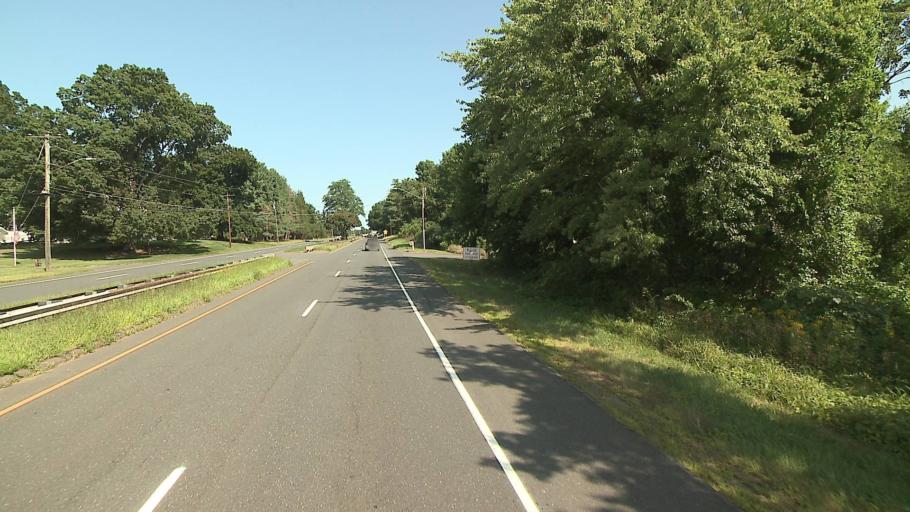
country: US
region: Connecticut
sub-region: Hartford County
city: Windsor
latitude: 41.8638
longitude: -72.6041
